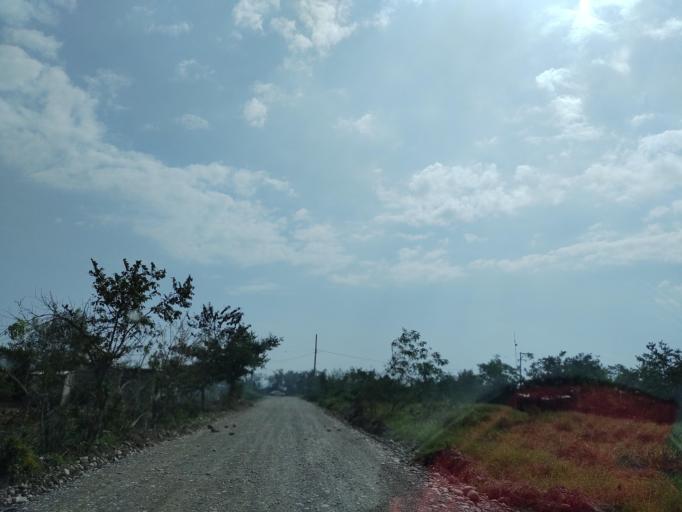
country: MX
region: Puebla
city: Espinal
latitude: 20.2811
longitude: -97.3324
